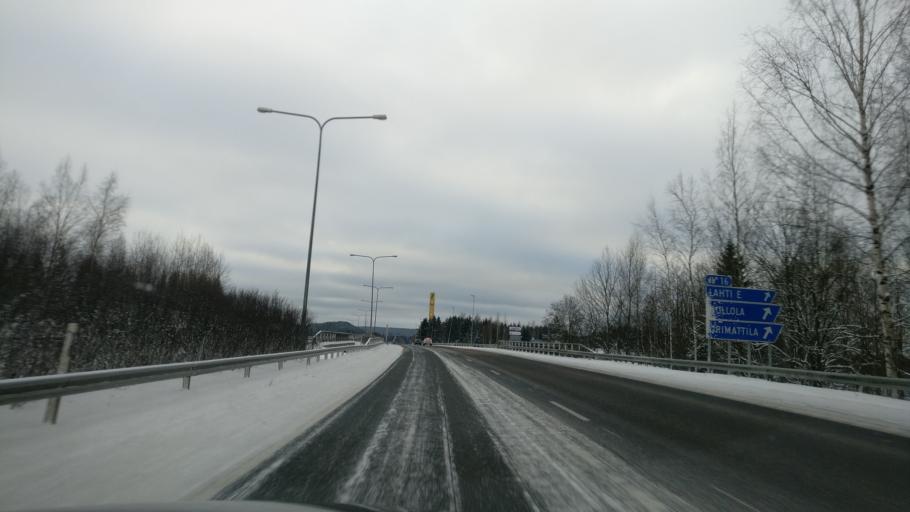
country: FI
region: Paijanne Tavastia
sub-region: Lahti
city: Lahti
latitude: 60.9370
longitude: 25.6450
